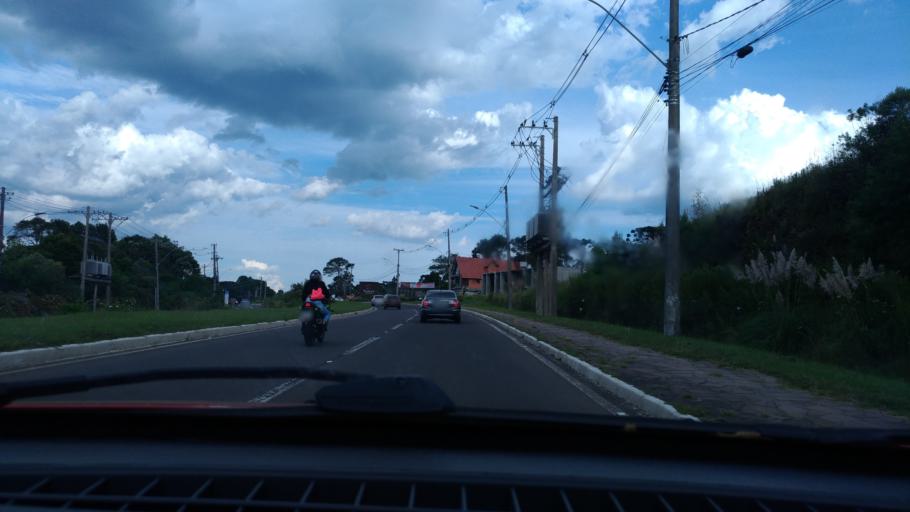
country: BR
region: Rio Grande do Sul
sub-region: Canela
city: Canela
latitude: -29.3598
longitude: -50.8405
